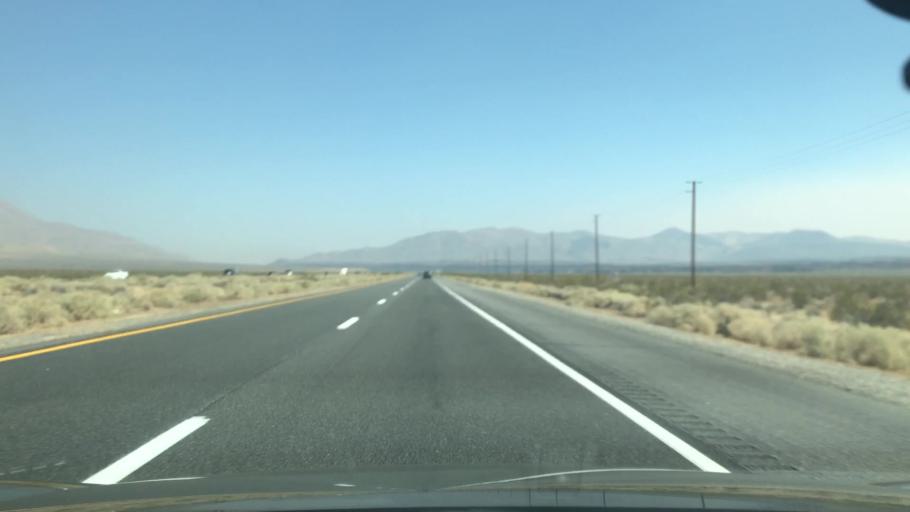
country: US
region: California
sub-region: Kern County
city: Inyokern
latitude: 35.8211
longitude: -117.8737
